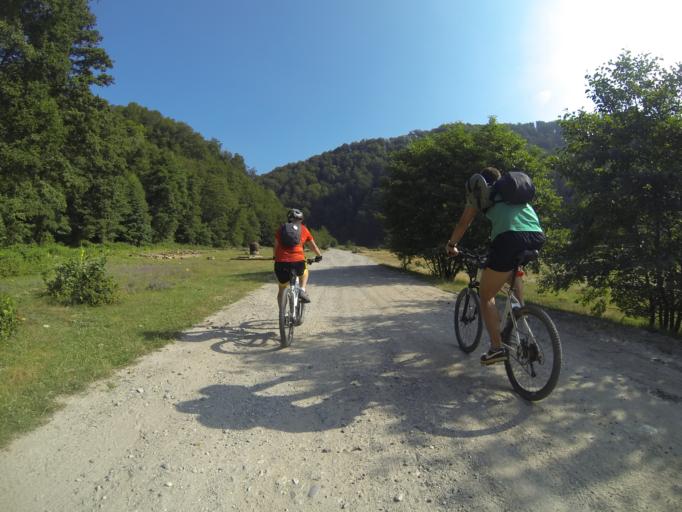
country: RO
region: Valcea
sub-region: Comuna Costesti
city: Bistrita
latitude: 45.2032
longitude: 23.9988
